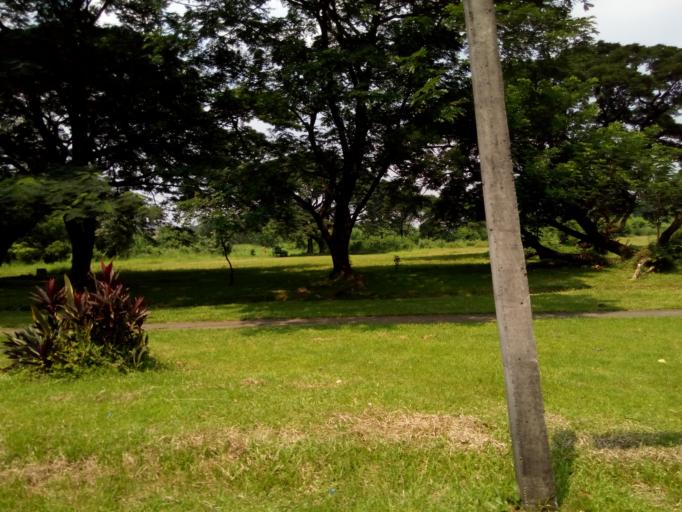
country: PH
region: Metro Manila
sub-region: Quezon City
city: Quezon City
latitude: 14.6550
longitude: 121.0587
